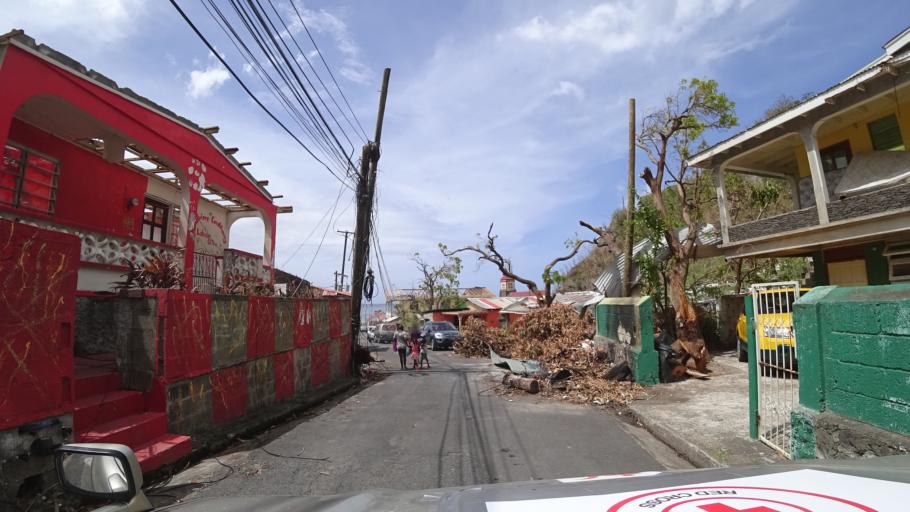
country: DM
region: Saint Mark
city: Soufriere
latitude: 15.2334
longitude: -61.3605
